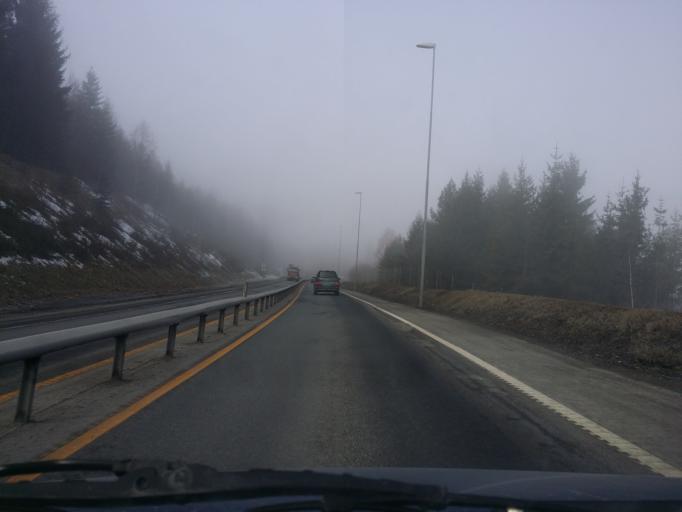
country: NO
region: Buskerud
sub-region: Drammen
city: Drammen
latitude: 59.7401
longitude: 10.1452
